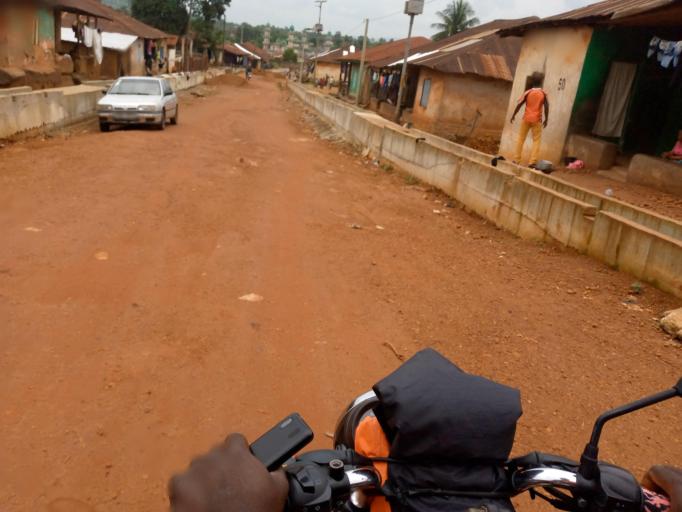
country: SL
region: Eastern Province
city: Kenema
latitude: 7.8717
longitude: -11.1888
